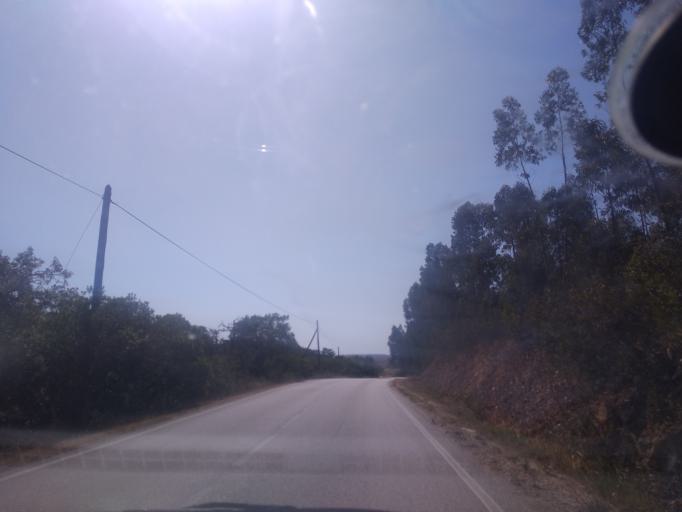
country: PT
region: Faro
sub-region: Aljezur
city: Aljezur
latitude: 37.2225
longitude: -8.8049
